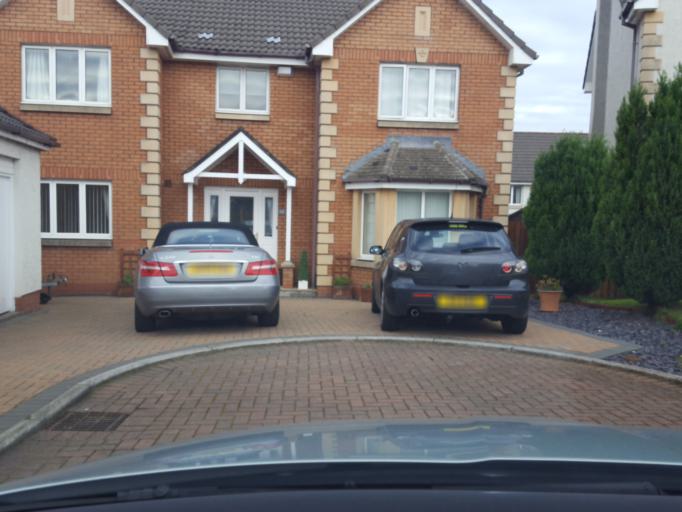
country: GB
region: Scotland
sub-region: West Lothian
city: Livingston
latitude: 55.8709
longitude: -3.5280
